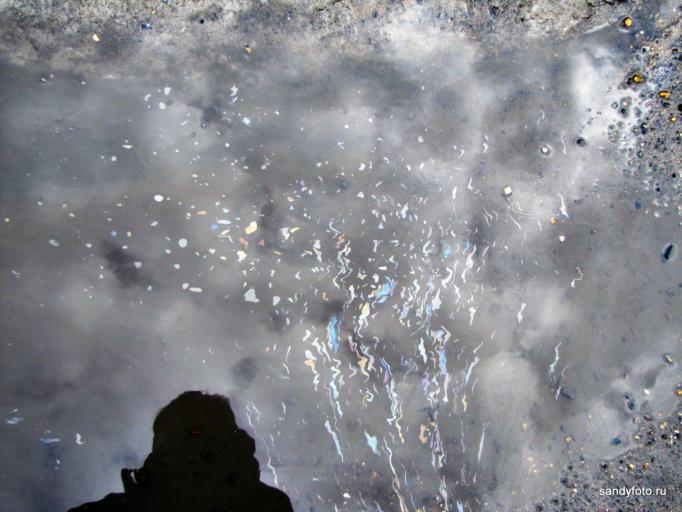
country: RU
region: Chelyabinsk
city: Troitsk
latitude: 54.1062
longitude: 61.5597
